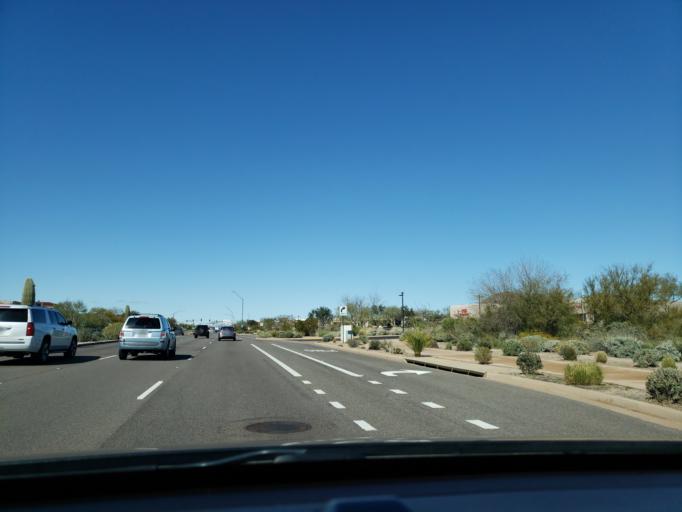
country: US
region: Arizona
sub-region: Maricopa County
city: Carefree
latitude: 33.6954
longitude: -111.8904
